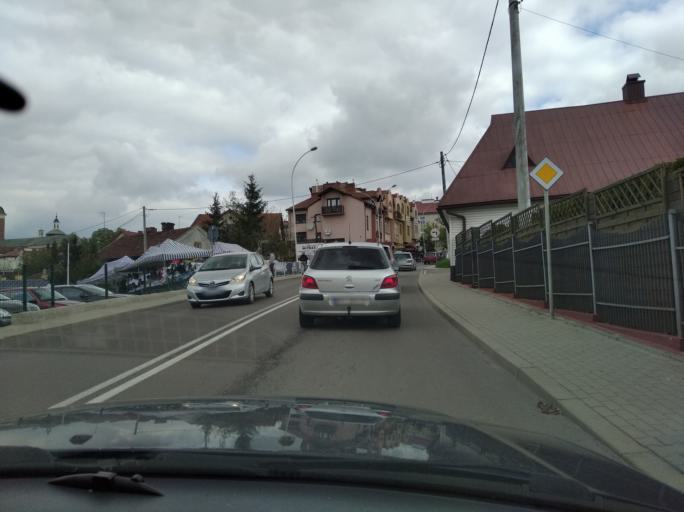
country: PL
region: Subcarpathian Voivodeship
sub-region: Powiat przeworski
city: Przeworsk
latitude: 50.0555
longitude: 22.4922
